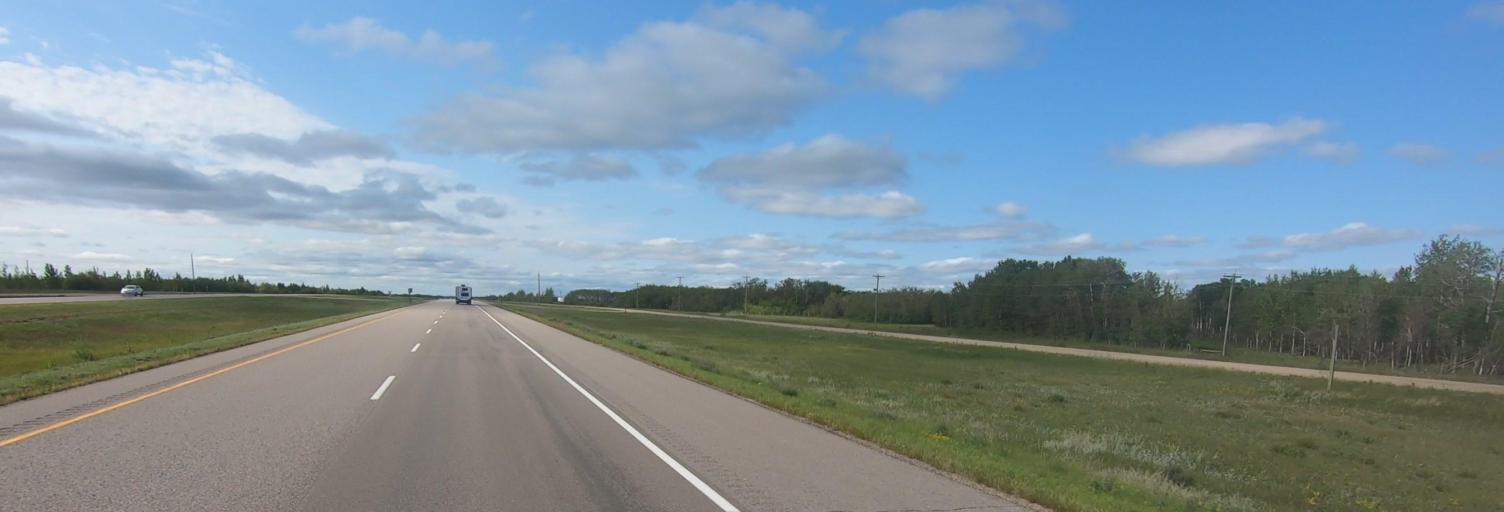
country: CA
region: Manitoba
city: Virden
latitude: 49.8089
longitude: -100.8458
